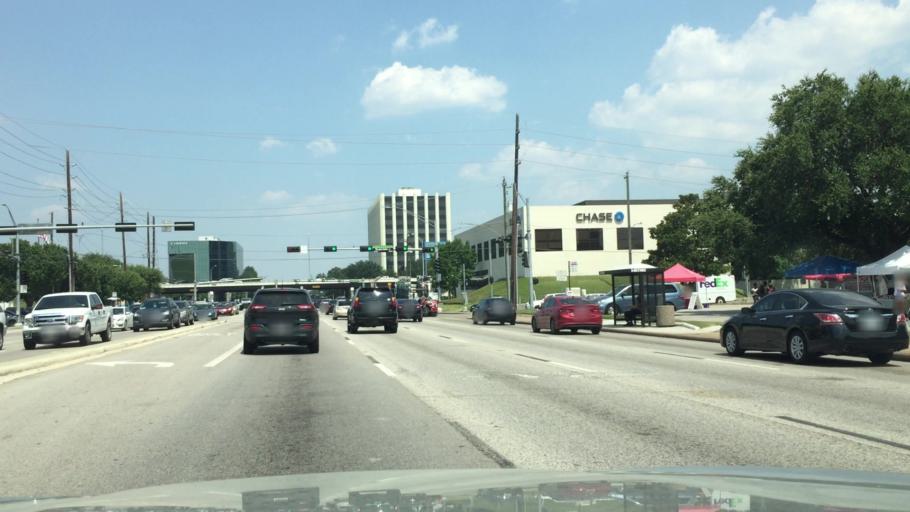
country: US
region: Texas
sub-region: Harris County
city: Bunker Hill Village
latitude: 29.7368
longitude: -95.5610
